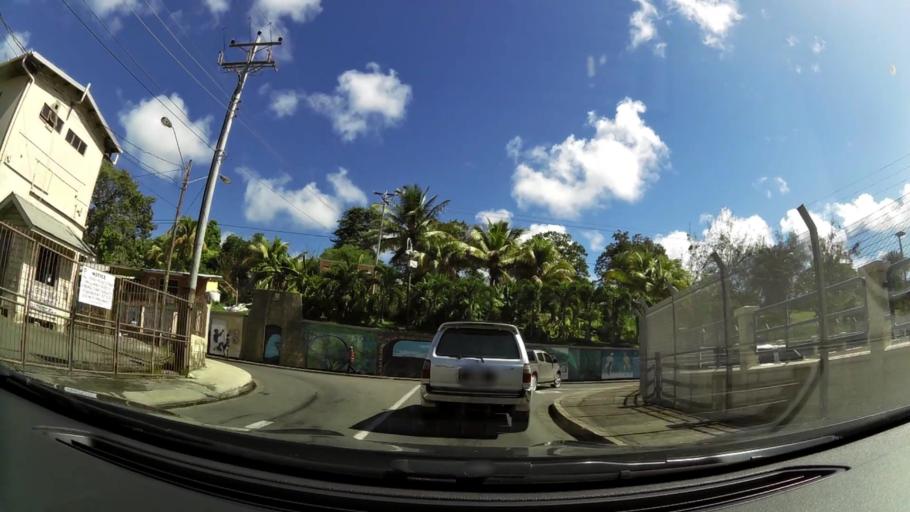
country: TT
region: Tobago
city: Scarborough
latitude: 11.1850
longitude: -60.7370
